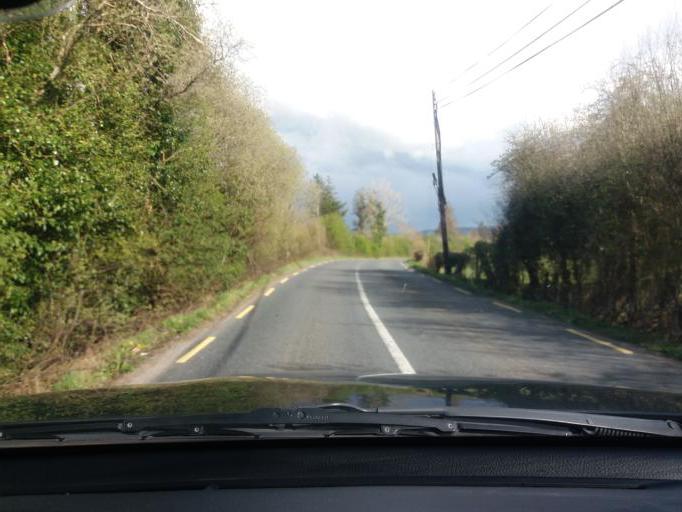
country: IE
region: Connaught
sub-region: County Leitrim
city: Manorhamilton
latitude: 54.3418
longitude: -8.2277
